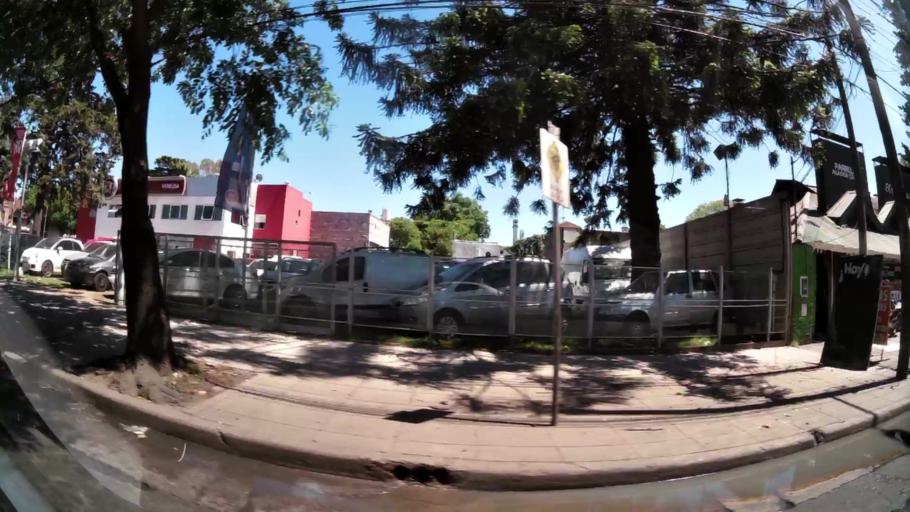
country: AR
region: Buenos Aires
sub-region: Partido de Tigre
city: Tigre
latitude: -34.4898
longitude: -58.6235
